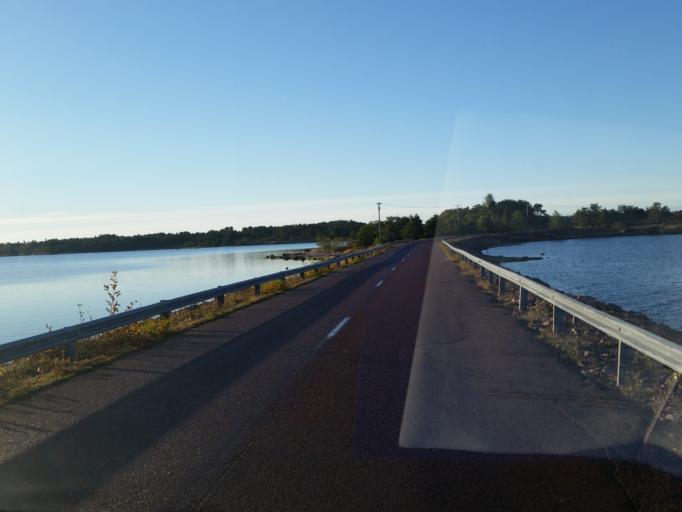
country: AX
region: Alands skaergard
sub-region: Vardoe
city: Vardoe
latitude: 60.3167
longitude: 20.3756
